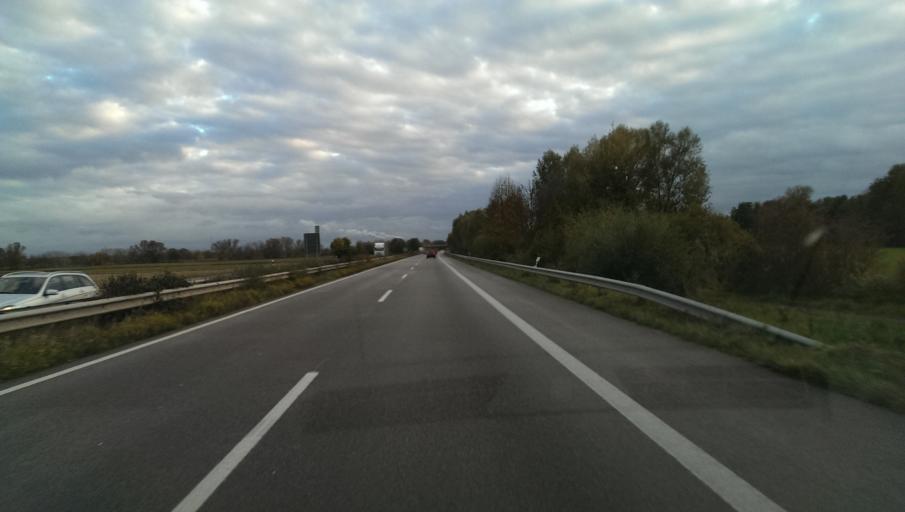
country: DE
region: Rheinland-Pfalz
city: Neupotz
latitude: 49.1157
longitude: 8.3066
